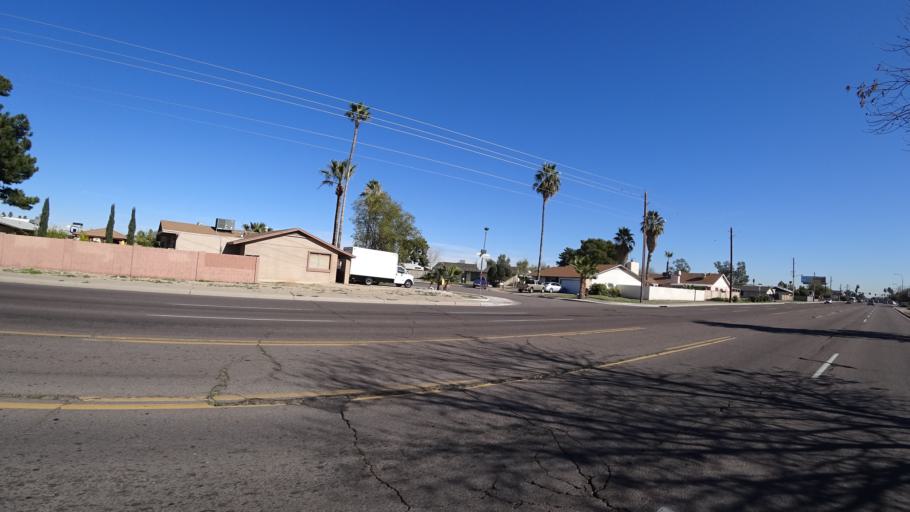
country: US
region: Arizona
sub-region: Maricopa County
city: Tolleson
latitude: 33.4942
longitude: -112.2419
